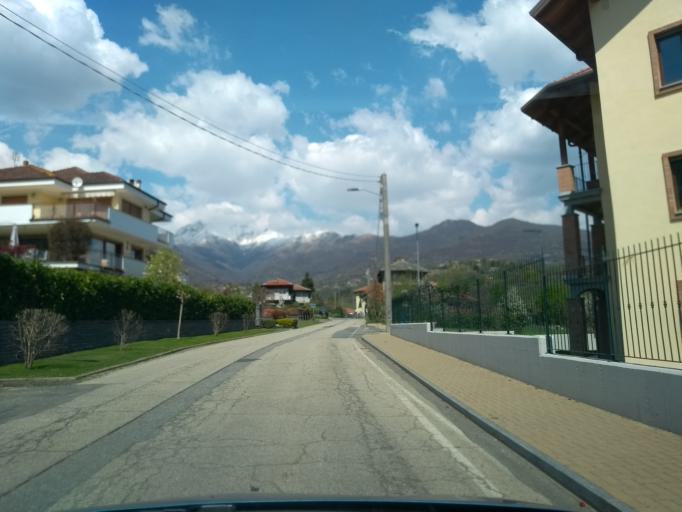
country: IT
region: Piedmont
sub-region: Provincia di Torino
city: Lanzo Torinese
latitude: 45.2802
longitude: 7.4697
